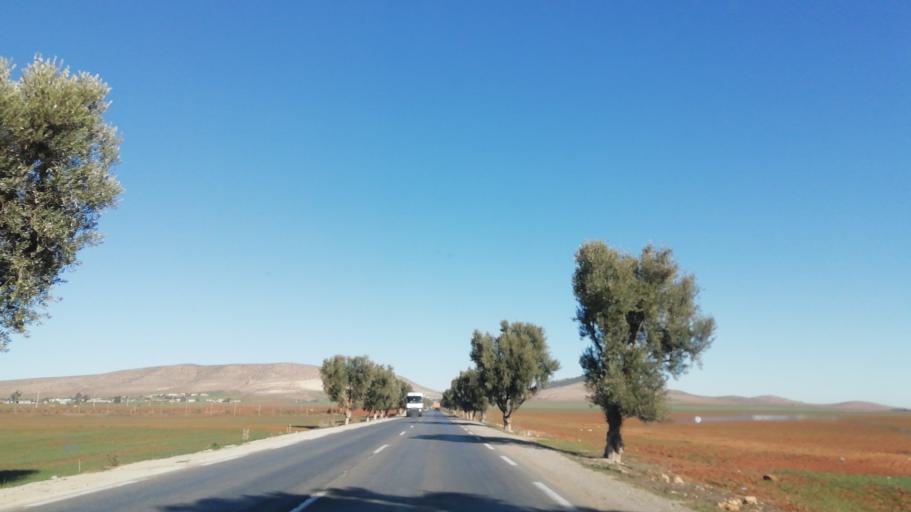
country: DZ
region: Mascara
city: Mascara
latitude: 35.2198
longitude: 0.1130
